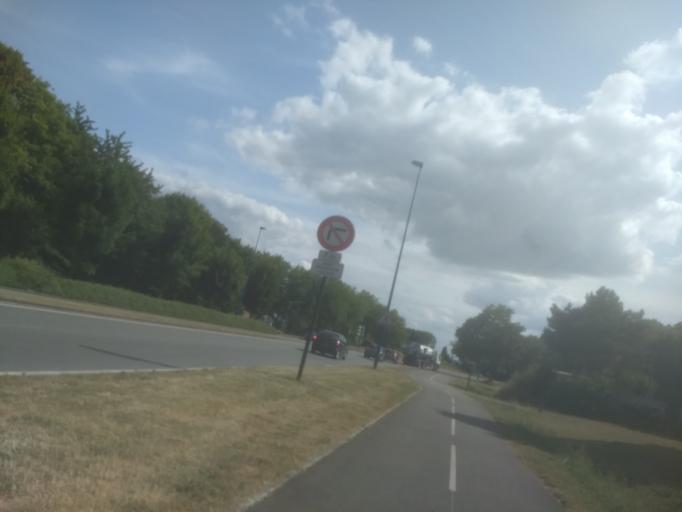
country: FR
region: Nord-Pas-de-Calais
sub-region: Departement du Pas-de-Calais
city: Beaurains
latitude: 50.2624
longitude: 2.7952
